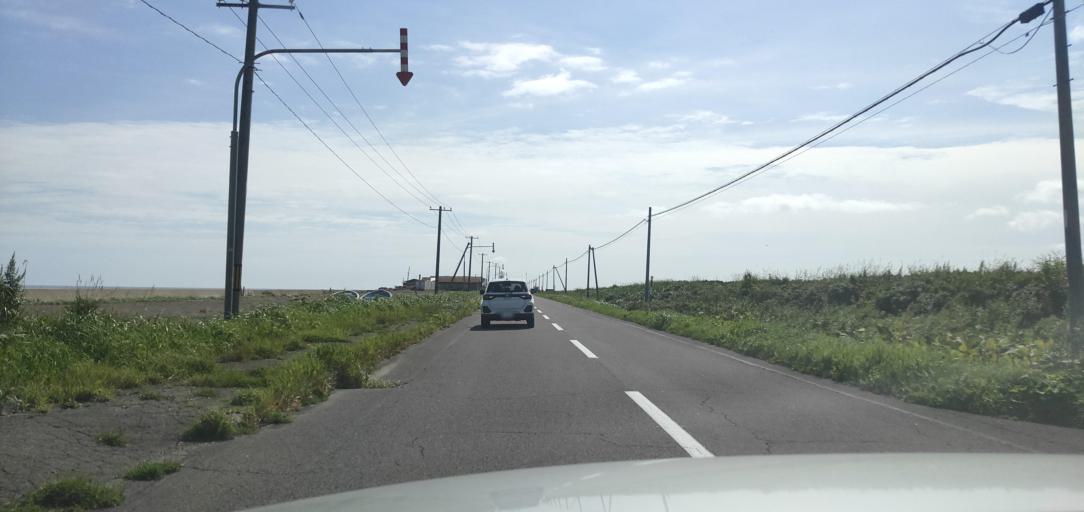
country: JP
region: Hokkaido
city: Shibetsu
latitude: 43.6367
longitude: 145.1699
